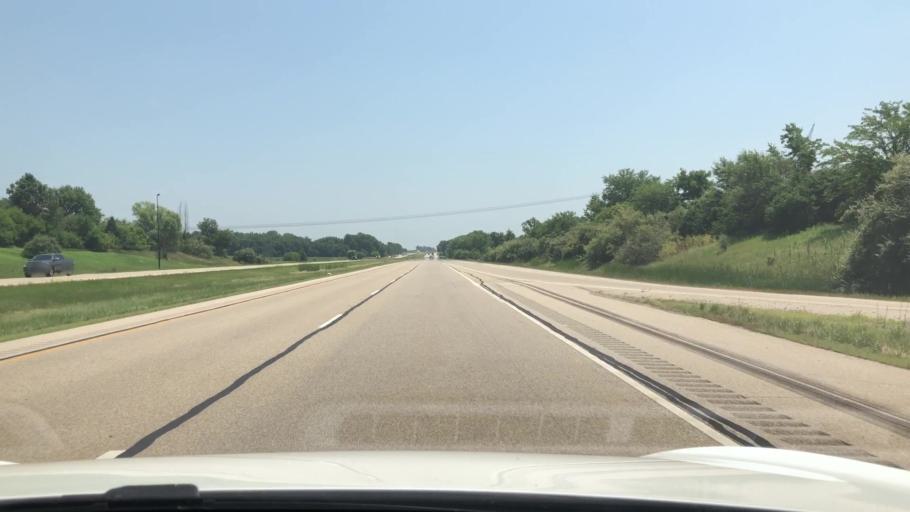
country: US
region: Illinois
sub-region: McLean County
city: Downs
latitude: 40.3884
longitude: -88.8729
